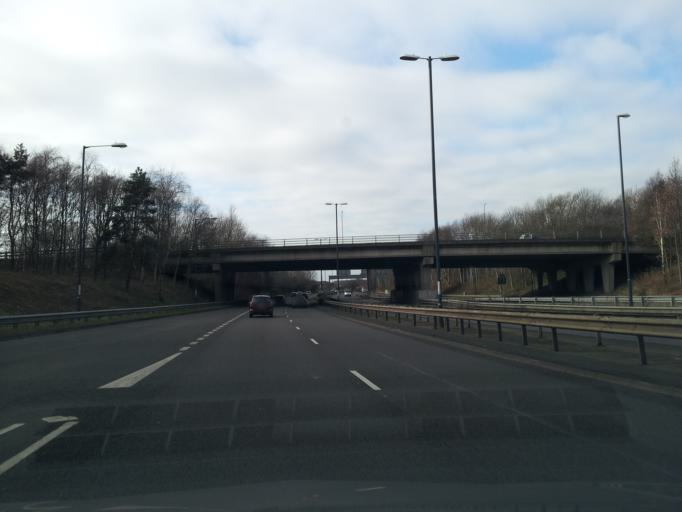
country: GB
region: England
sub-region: Derbyshire
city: Borrowash
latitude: 52.9149
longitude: -1.4215
